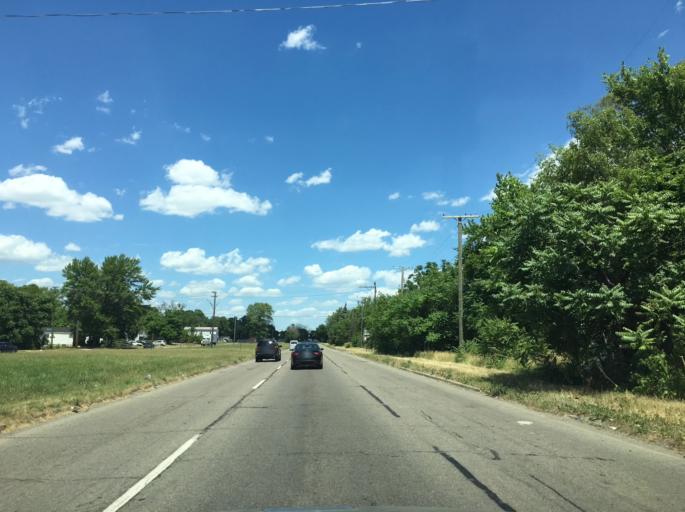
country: US
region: Michigan
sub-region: Wayne County
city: Hamtramck
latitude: 42.4271
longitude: -83.0431
